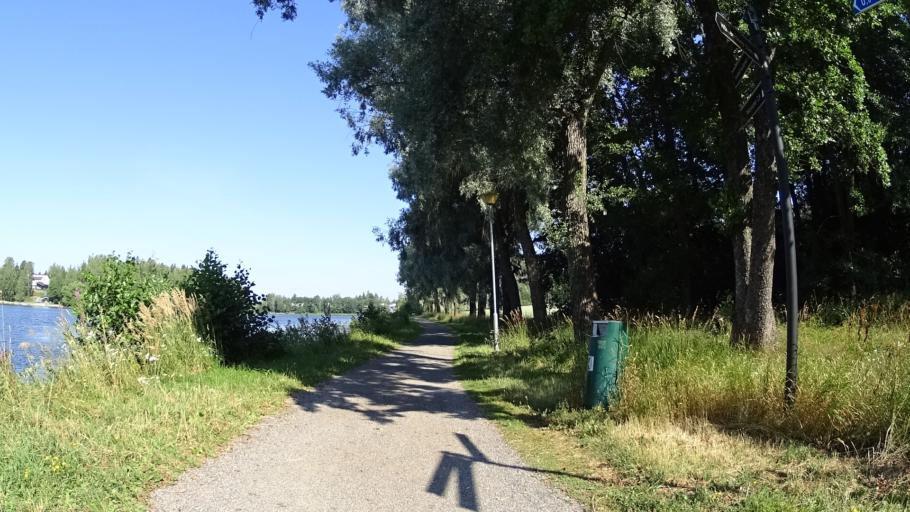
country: FI
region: Haeme
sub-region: Haemeenlinna
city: Haemeenlinna
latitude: 61.0161
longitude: 24.4498
